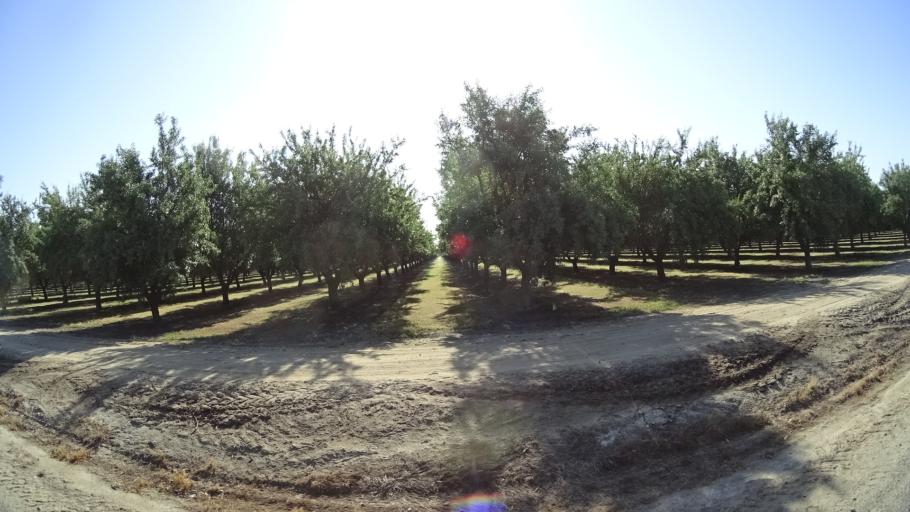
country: US
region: California
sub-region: Fresno County
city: Laton
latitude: 36.3960
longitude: -119.7181
